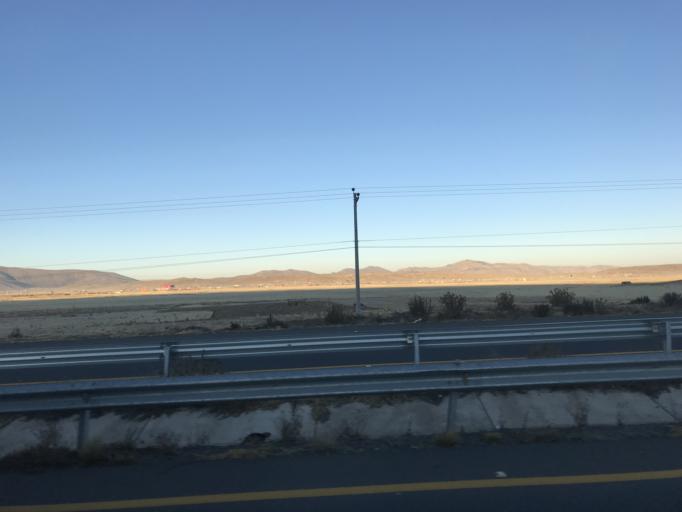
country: BO
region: La Paz
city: Batallas
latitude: -16.2871
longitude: -68.5442
